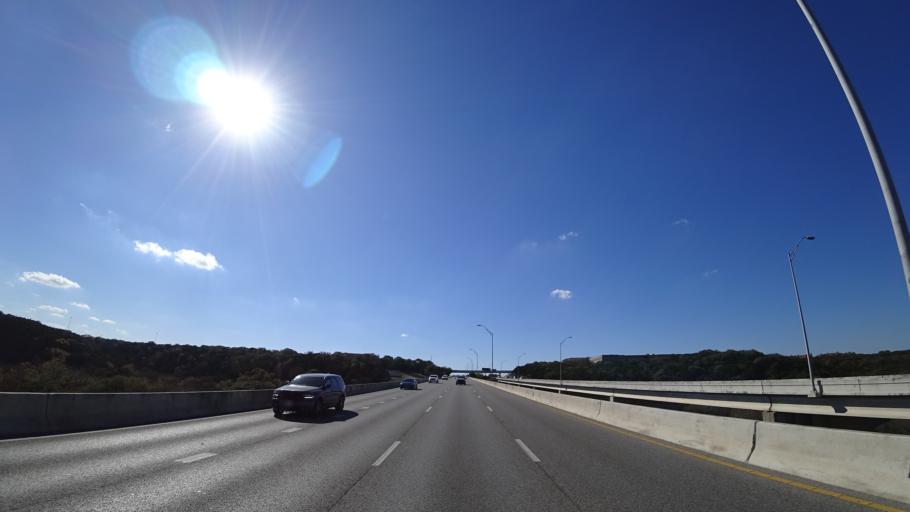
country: US
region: Texas
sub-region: Travis County
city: Rollingwood
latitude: 30.2427
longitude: -97.8109
